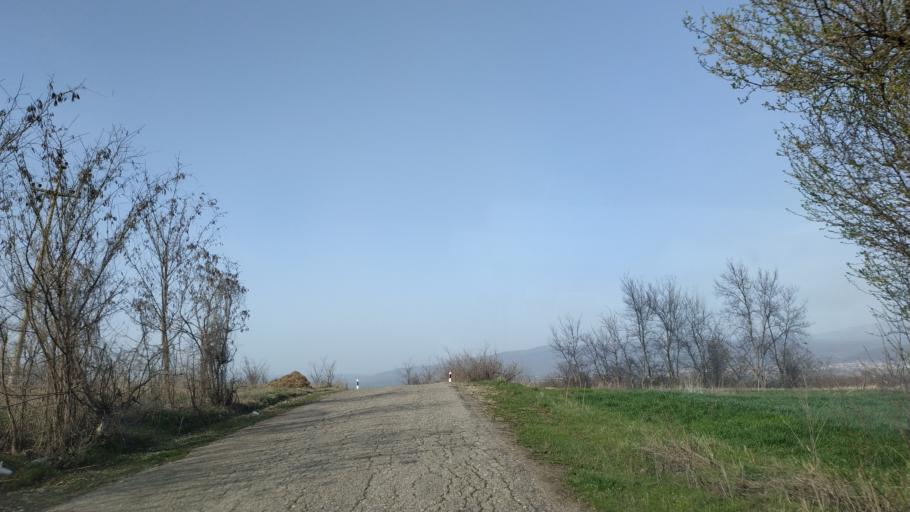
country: RS
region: Central Serbia
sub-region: Nisavski Okrug
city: Aleksinac
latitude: 43.5135
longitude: 21.6477
